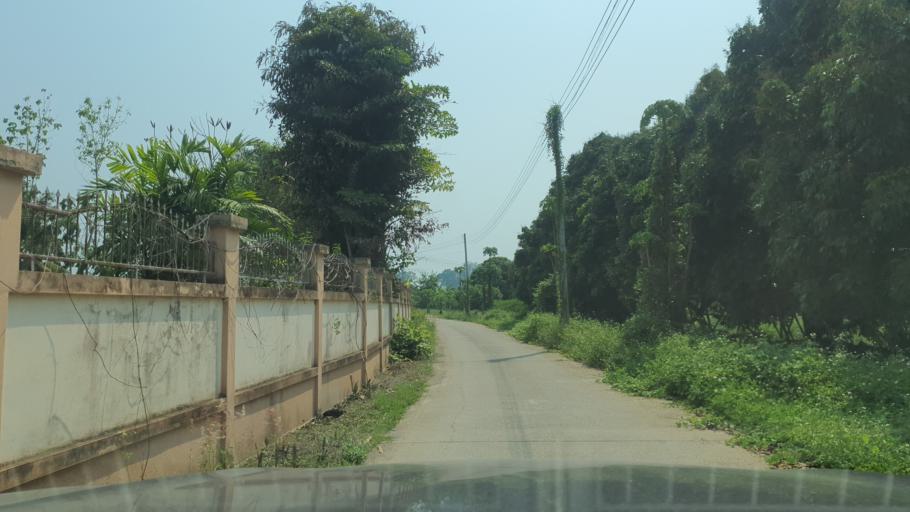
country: TH
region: Chiang Mai
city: Saraphi
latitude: 18.6682
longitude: 98.9917
